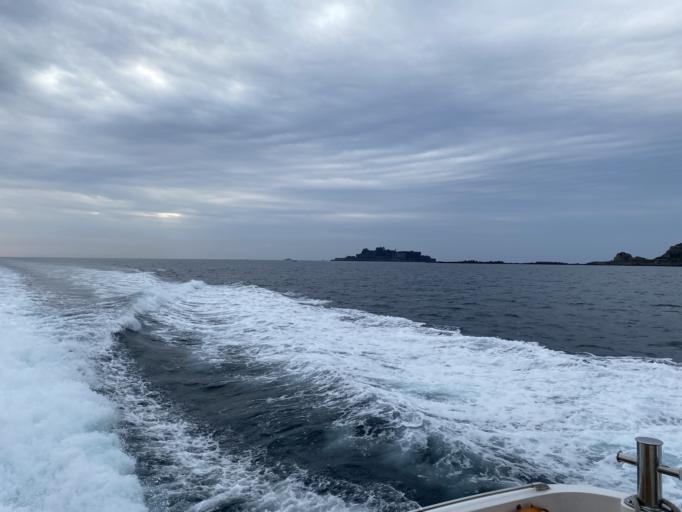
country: JP
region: Nagasaki
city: Nagasaki-shi
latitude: 32.6333
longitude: 129.7570
